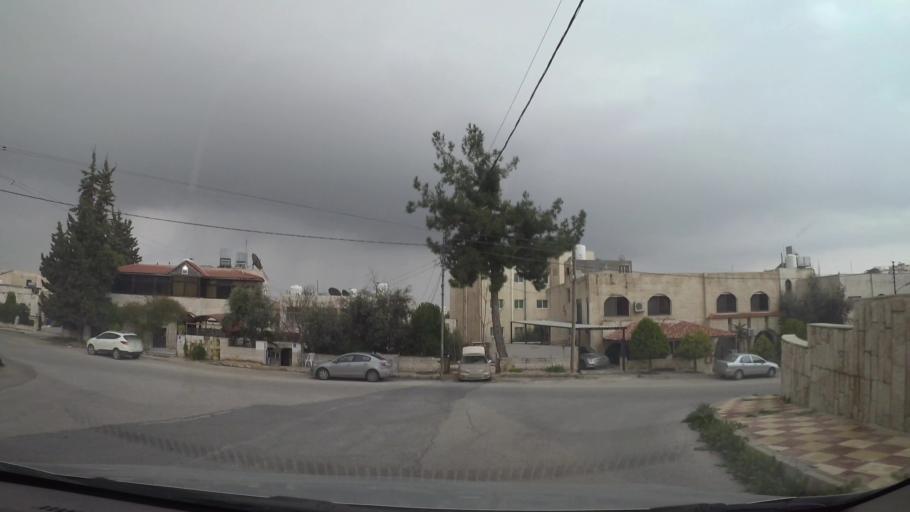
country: JO
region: Amman
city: Umm as Summaq
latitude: 31.8867
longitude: 35.8539
